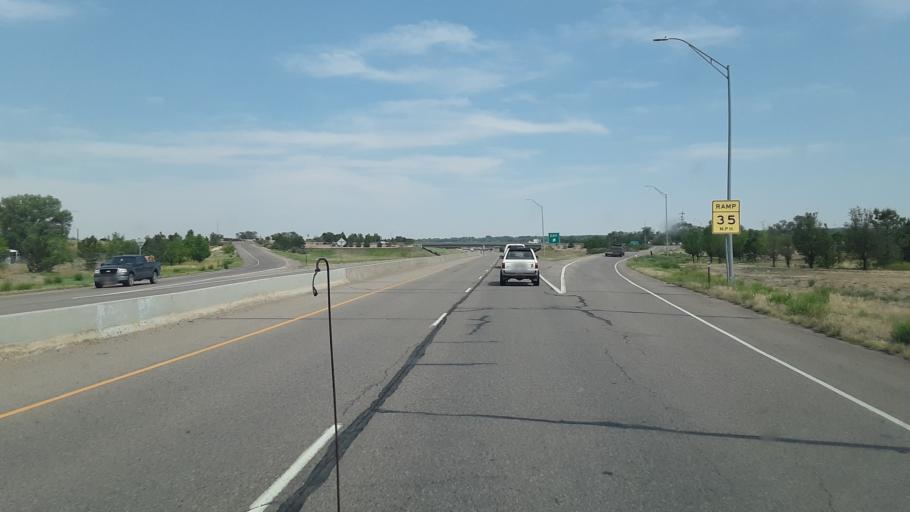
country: US
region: Colorado
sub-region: Pueblo County
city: Pueblo
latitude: 38.2769
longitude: -104.5620
